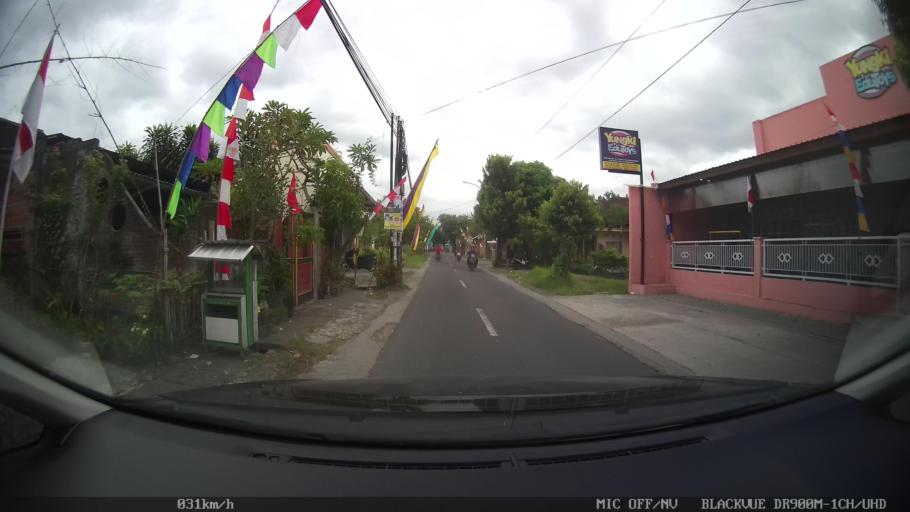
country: ID
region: Daerah Istimewa Yogyakarta
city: Depok
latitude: -7.8110
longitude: 110.4182
